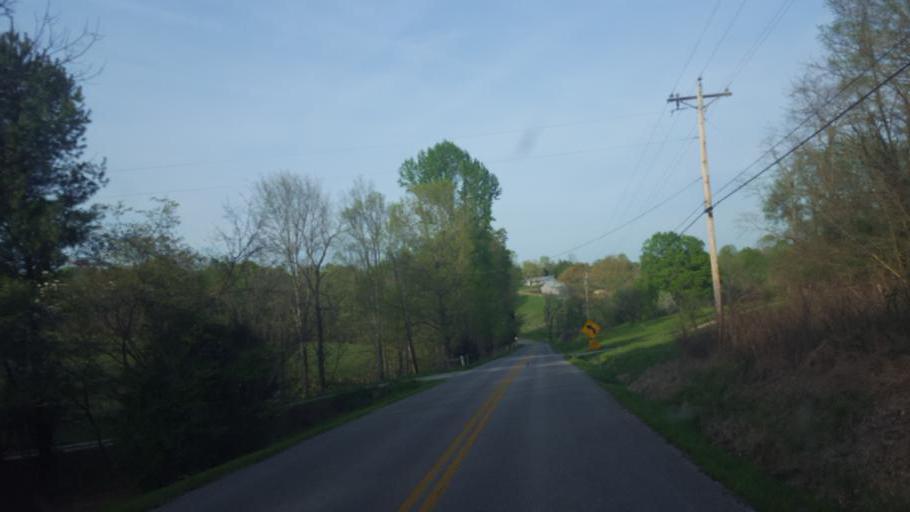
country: US
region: Kentucky
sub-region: Allen County
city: Scottsville
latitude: 36.9243
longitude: -86.0967
